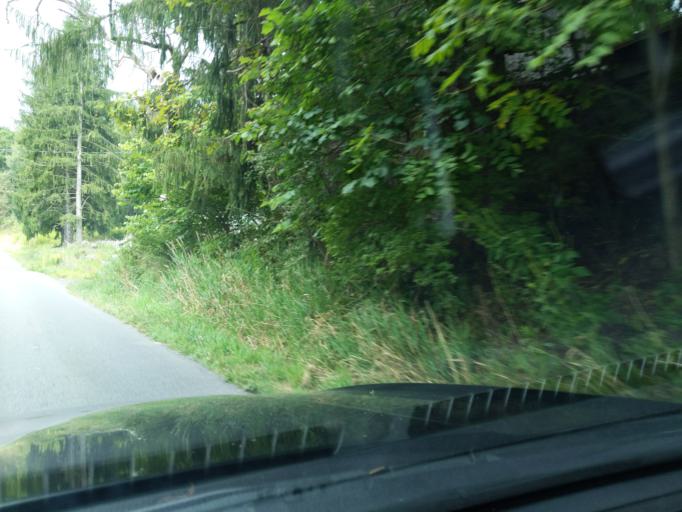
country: US
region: Pennsylvania
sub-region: Blair County
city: Claysburg
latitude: 40.3543
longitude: -78.4504
